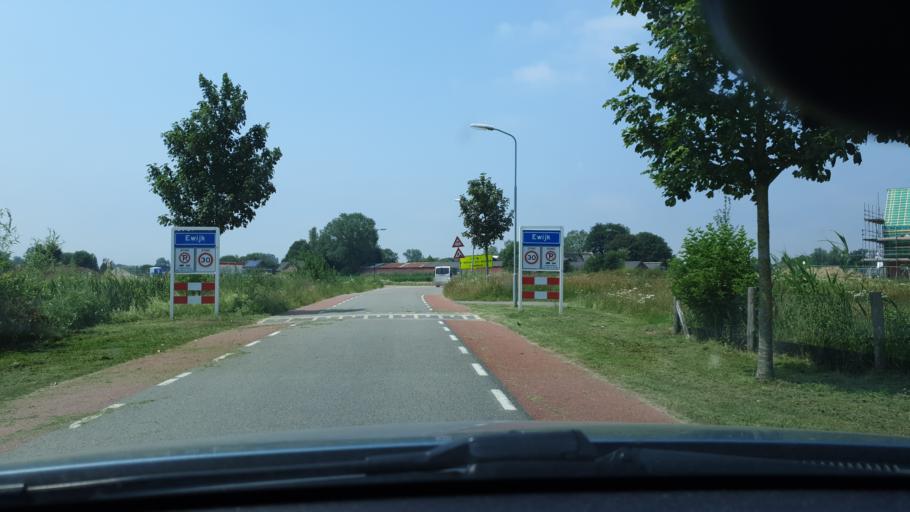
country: NL
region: Gelderland
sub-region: Gemeente Beuningen
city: Beuningen
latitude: 51.8632
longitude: 5.7476
